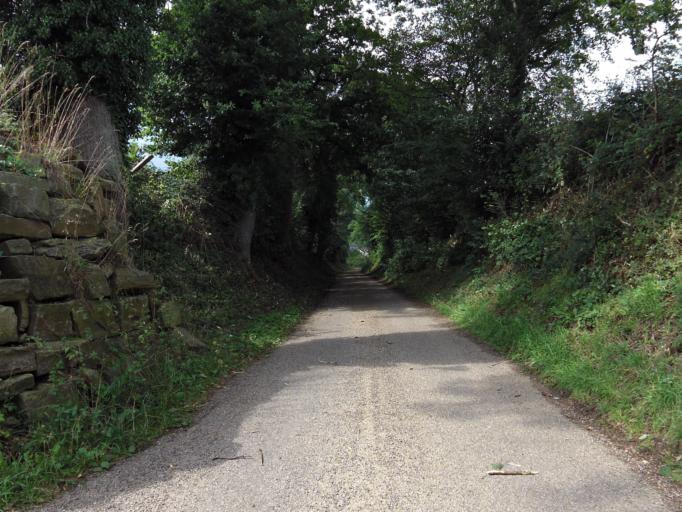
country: NL
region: Limburg
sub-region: Gemeente Simpelveld
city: Simpelveld
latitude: 50.8343
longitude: 5.9969
